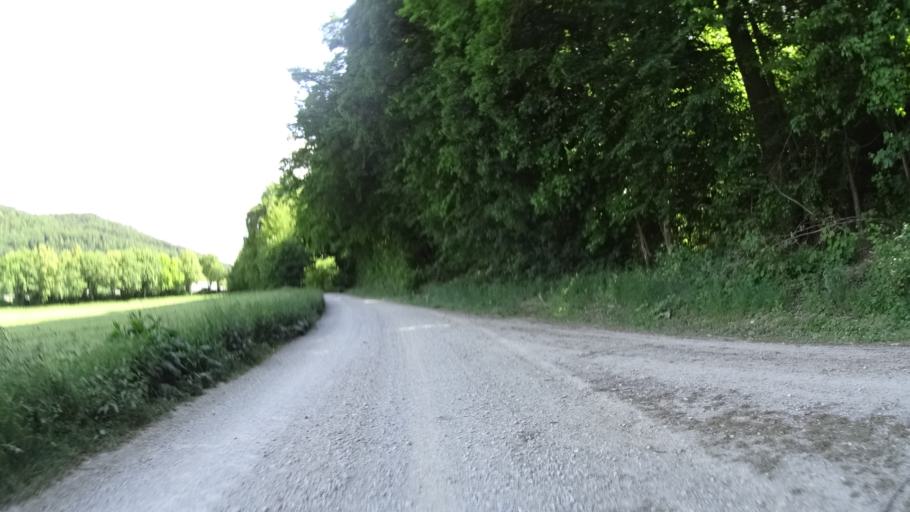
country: DE
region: Bavaria
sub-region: Regierungsbezirk Mittelfranken
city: Greding
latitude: 49.0157
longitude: 11.3557
